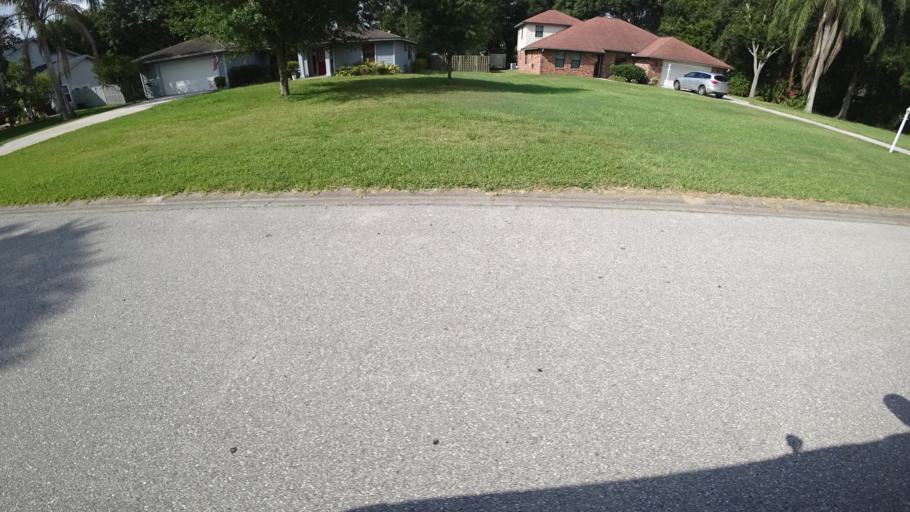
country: US
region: Florida
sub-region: Sarasota County
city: The Meadows
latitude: 27.4347
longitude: -82.4437
